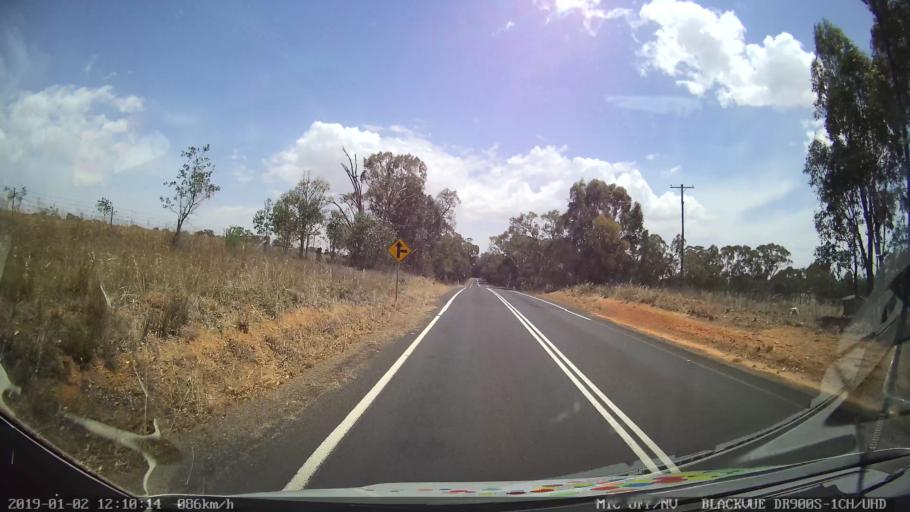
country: AU
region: New South Wales
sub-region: Young
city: Young
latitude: -34.4626
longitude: 148.2649
